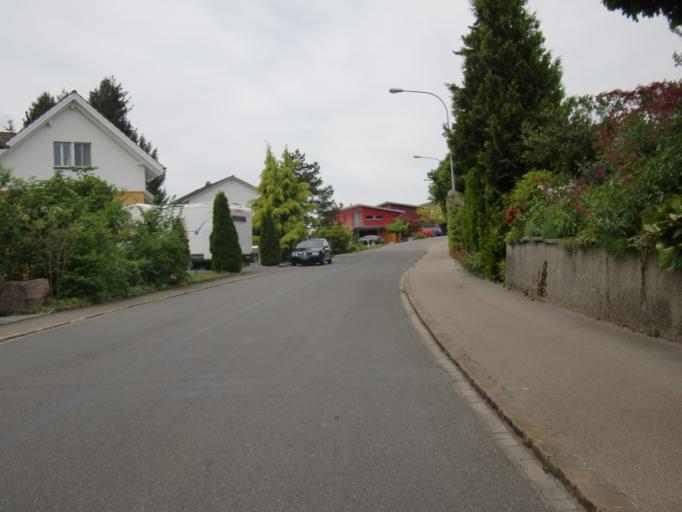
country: CH
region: Zurich
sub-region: Bezirk Hinwil
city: Tann
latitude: 47.2678
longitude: 8.8399
